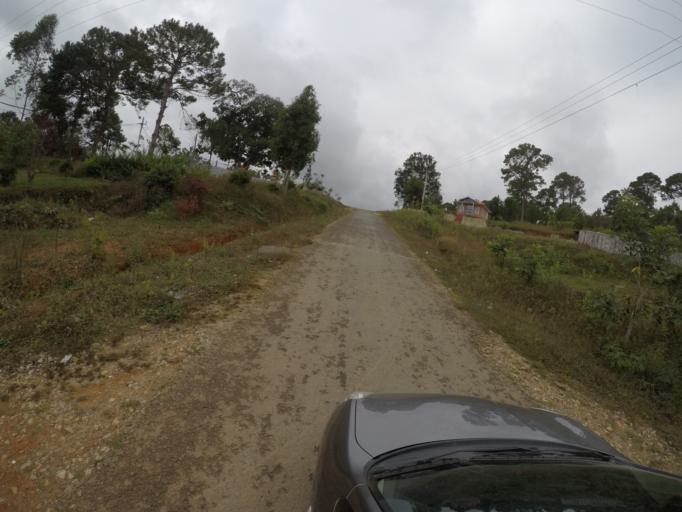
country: MM
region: Shan
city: Taunggyi
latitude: 20.6518
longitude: 96.6249
